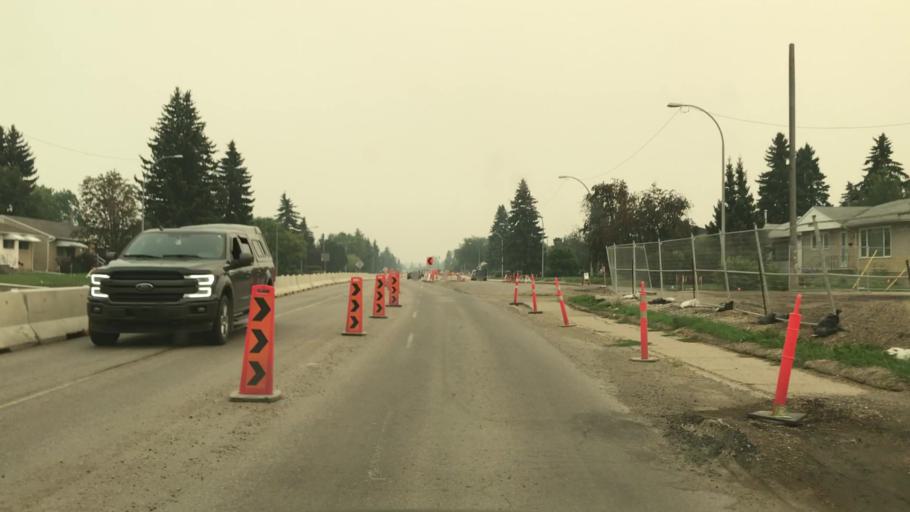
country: CA
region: Alberta
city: Edmonton
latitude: 53.5122
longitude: -113.4552
